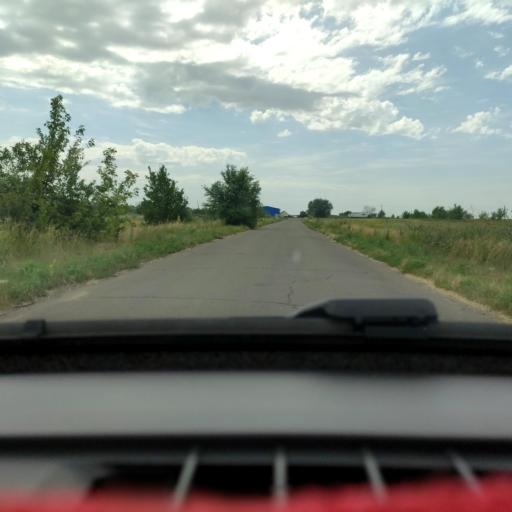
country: RU
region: Voronezj
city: Davydovka
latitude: 51.1948
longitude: 39.4928
